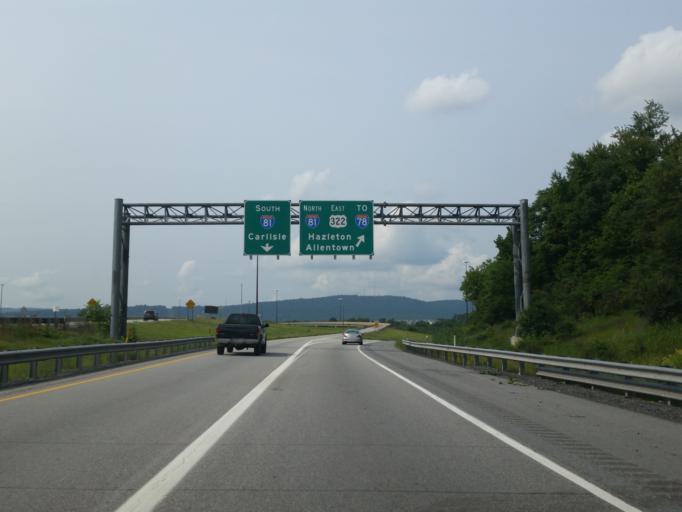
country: US
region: Pennsylvania
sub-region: Dauphin County
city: Harrisburg
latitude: 40.2981
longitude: -76.8805
